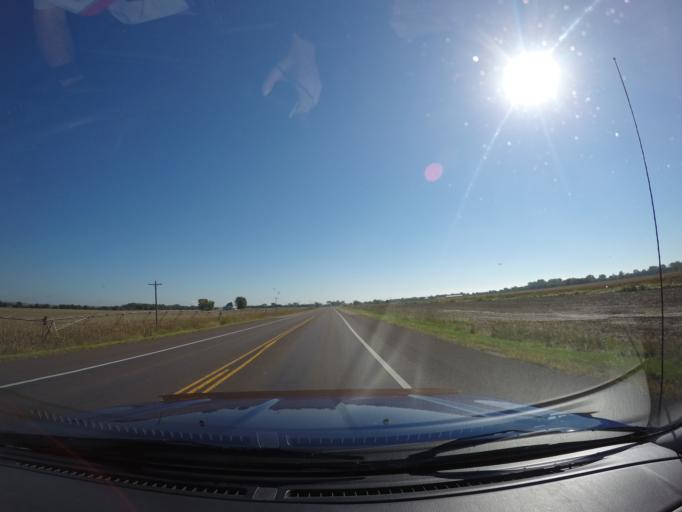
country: US
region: Kansas
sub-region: Pottawatomie County
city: Wamego
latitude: 39.2146
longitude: -96.2283
